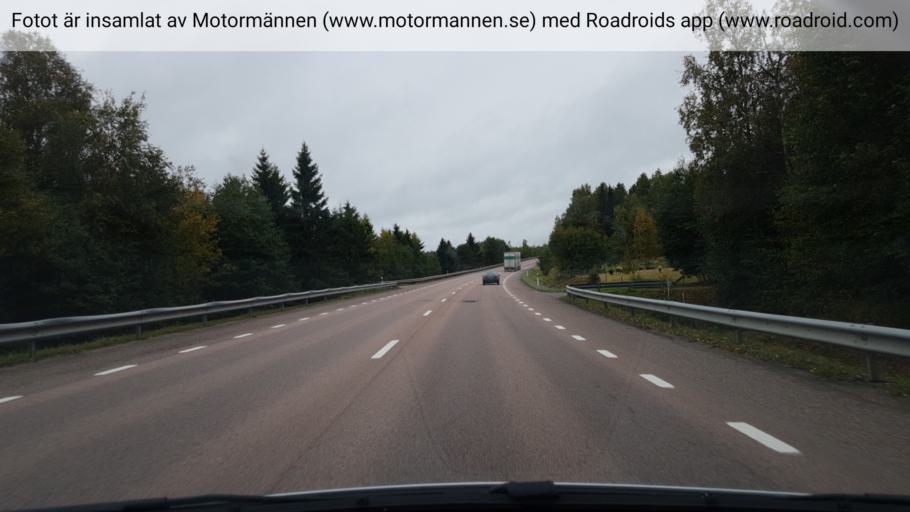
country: SE
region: Gaevleborg
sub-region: Nordanstigs Kommun
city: Bergsjoe
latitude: 62.0144
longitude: 17.2482
